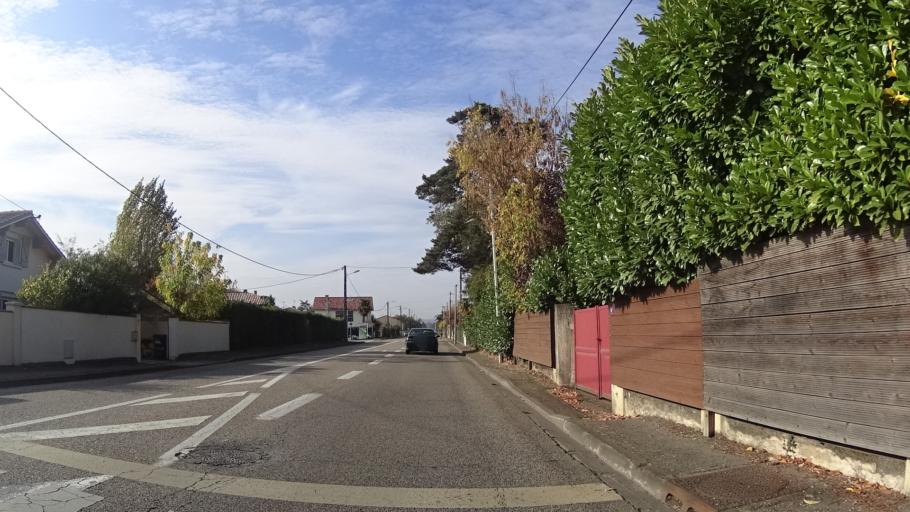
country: FR
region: Aquitaine
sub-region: Departement du Lot-et-Garonne
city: Le Passage
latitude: 44.1931
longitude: 0.5926
